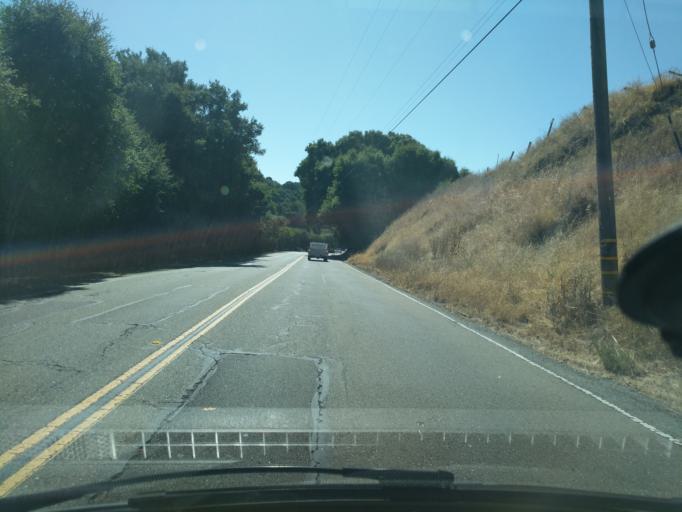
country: US
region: California
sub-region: Contra Costa County
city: San Ramon
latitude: 37.7677
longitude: -122.0091
